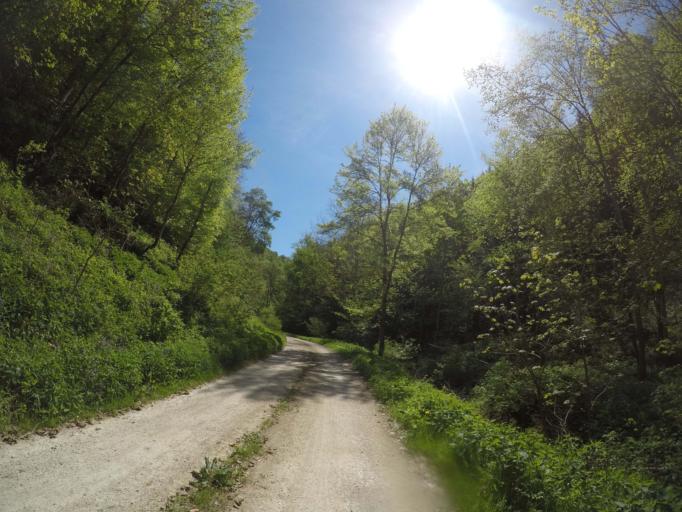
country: DE
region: Baden-Wuerttemberg
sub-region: Tuebingen Region
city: Schelklingen
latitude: 48.4047
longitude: 9.7296
